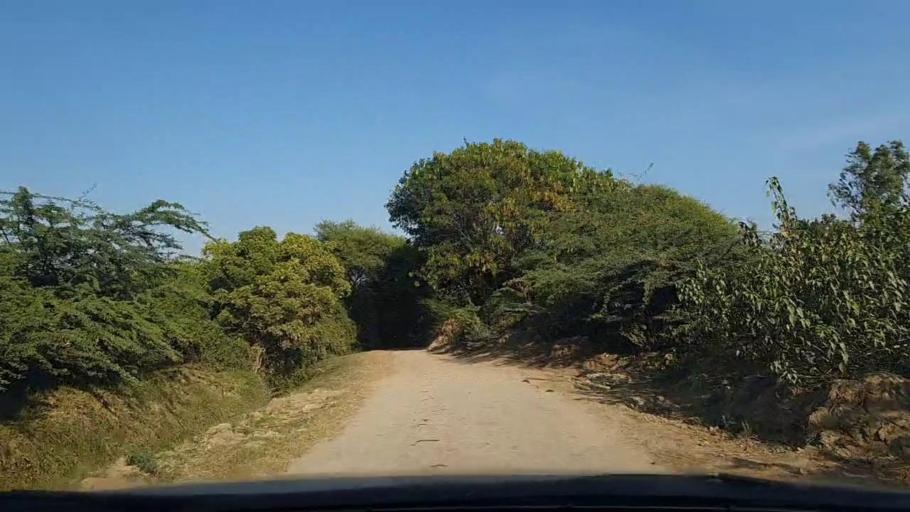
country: PK
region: Sindh
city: Mirpur Sakro
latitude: 24.5267
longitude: 67.6485
